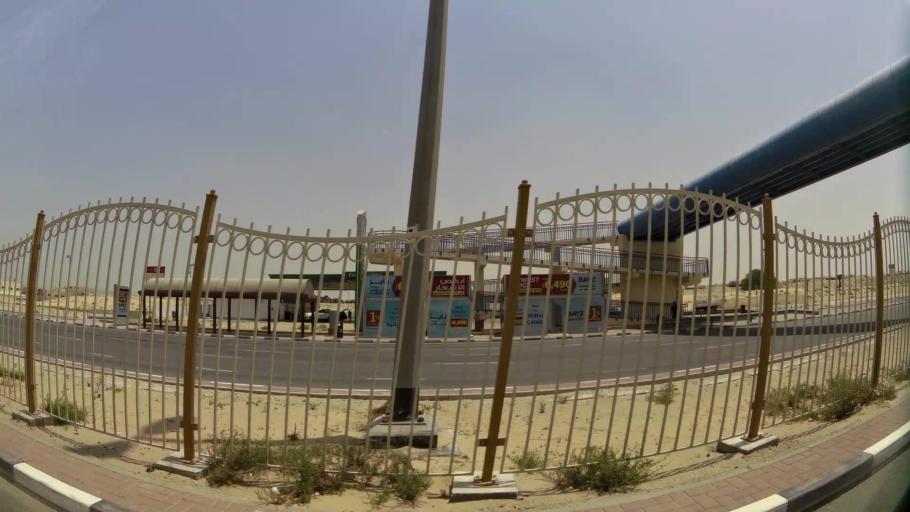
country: AE
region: Ash Shariqah
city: Sharjah
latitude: 25.2819
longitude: 55.4118
